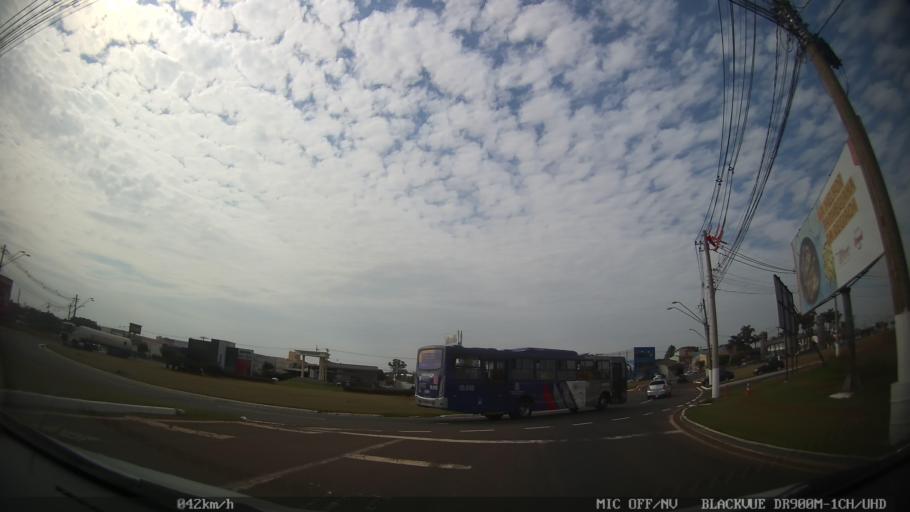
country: BR
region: Sao Paulo
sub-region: Paulinia
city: Paulinia
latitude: -22.7916
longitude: -47.1393
